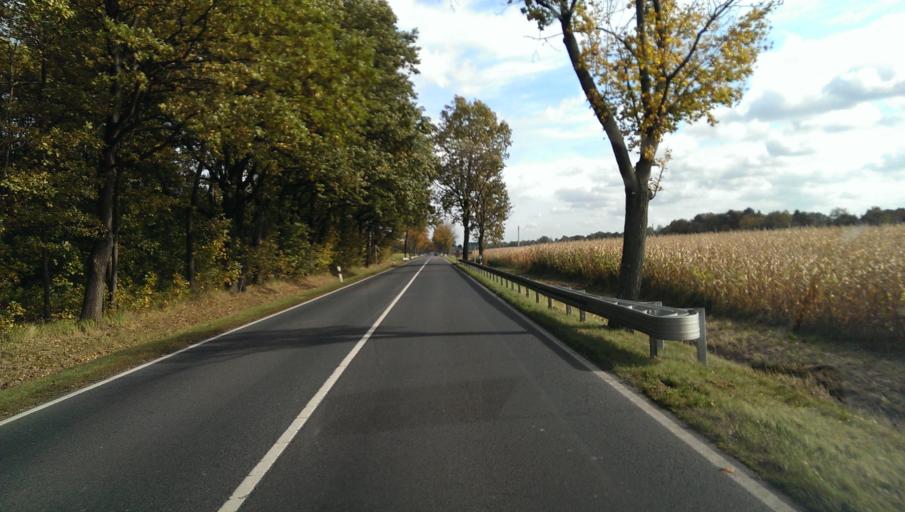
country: DE
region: Brandenburg
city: Lauchhammer
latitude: 51.4634
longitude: 13.7460
